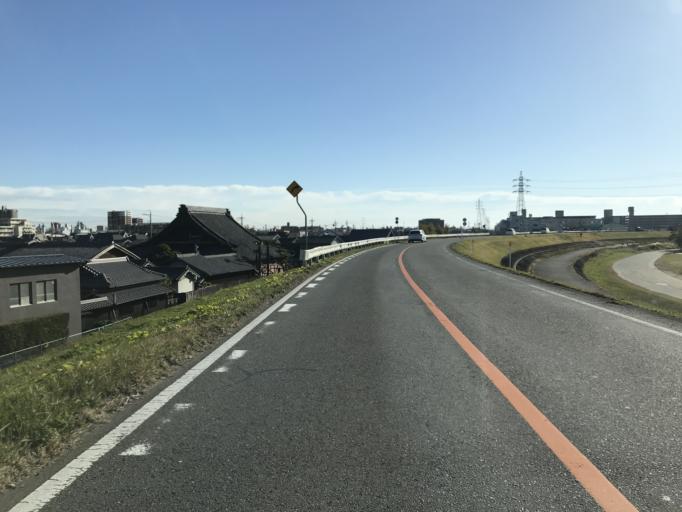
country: JP
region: Aichi
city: Kanie
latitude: 35.1553
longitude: 136.8399
